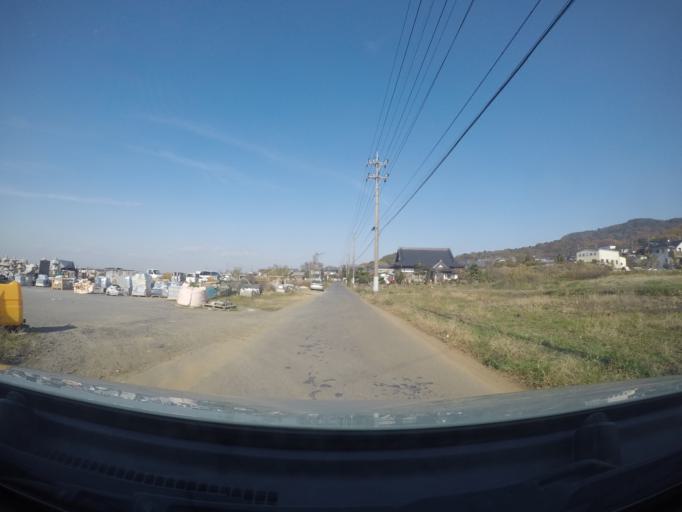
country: JP
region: Ibaraki
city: Tsukuba
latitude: 36.2302
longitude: 140.0656
